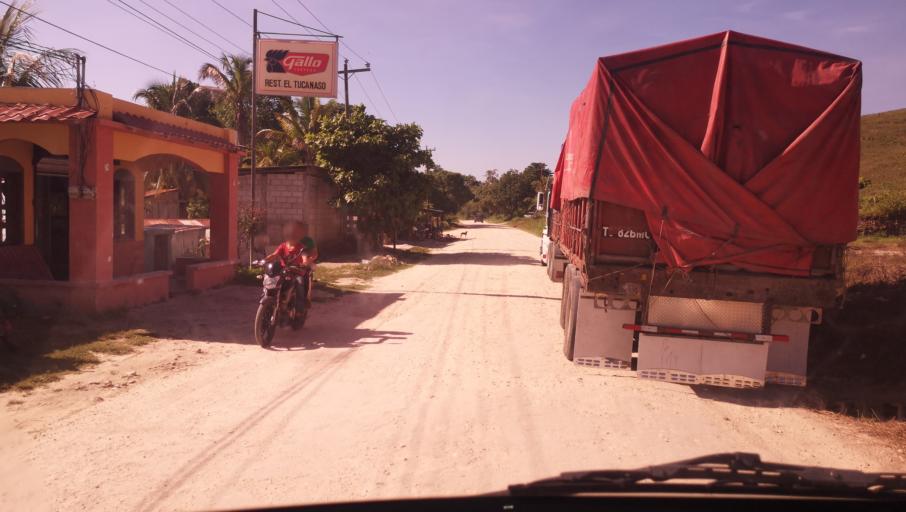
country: GT
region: Peten
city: Dolores
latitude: 16.7250
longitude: -89.3791
